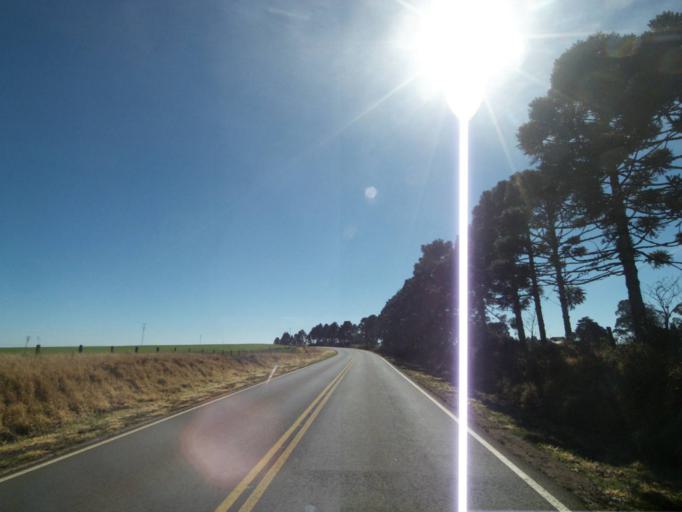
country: BR
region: Parana
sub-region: Castro
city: Castro
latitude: -24.6736
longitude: -50.2137
